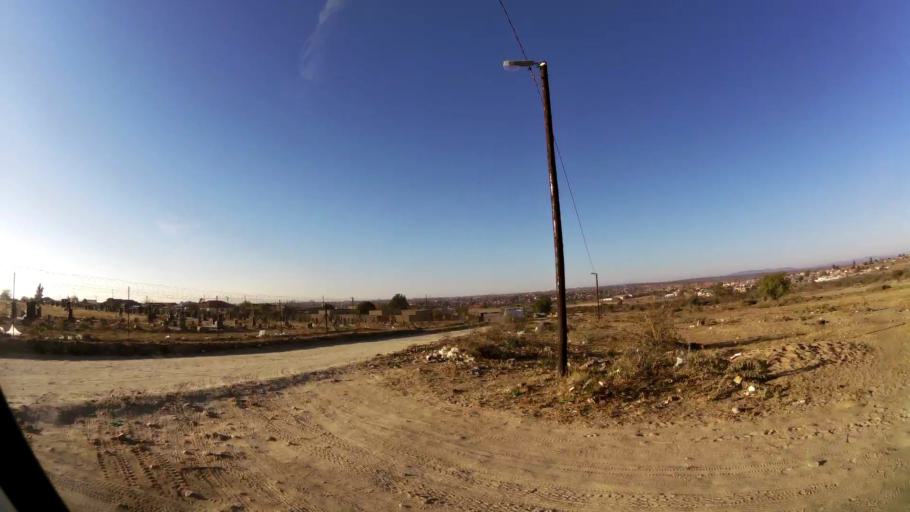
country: ZA
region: Limpopo
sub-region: Capricorn District Municipality
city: Polokwane
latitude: -23.8381
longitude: 29.3587
